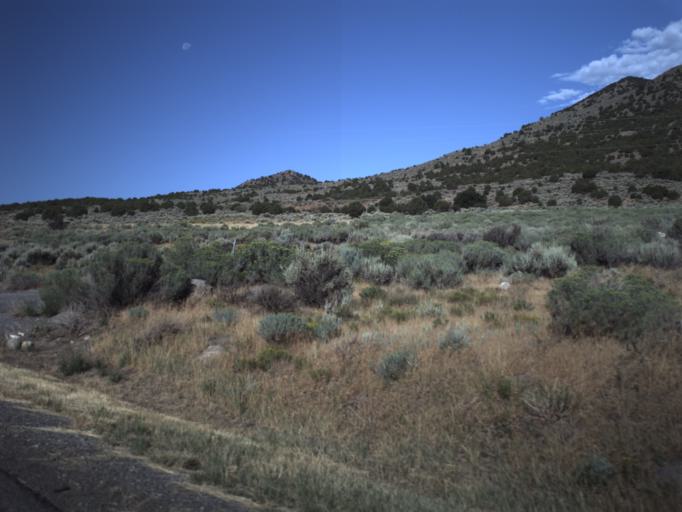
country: US
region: Utah
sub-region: Utah County
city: Genola
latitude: 39.9698
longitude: -112.0876
